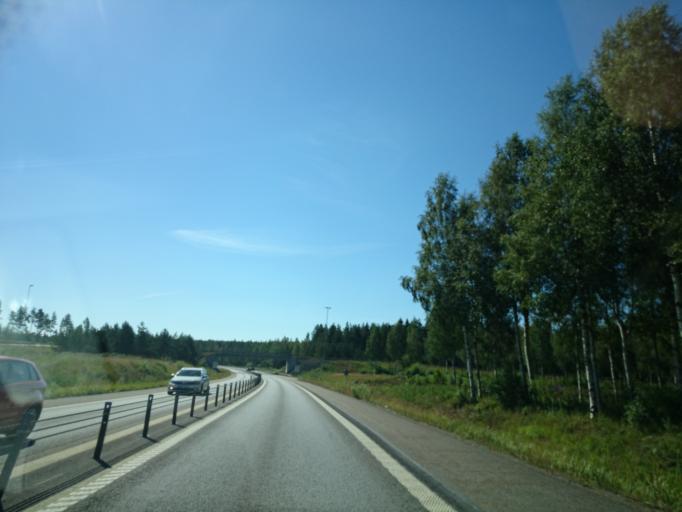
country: SE
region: Gaevleborg
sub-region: Gavle Kommun
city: Norrsundet
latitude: 60.9036
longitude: 17.0162
